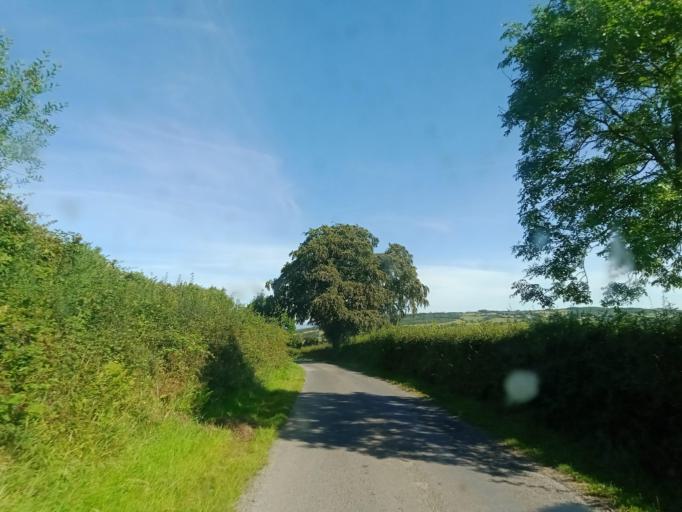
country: IE
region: Leinster
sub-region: Kilkenny
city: Ballyragget
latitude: 52.7953
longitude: -7.4247
